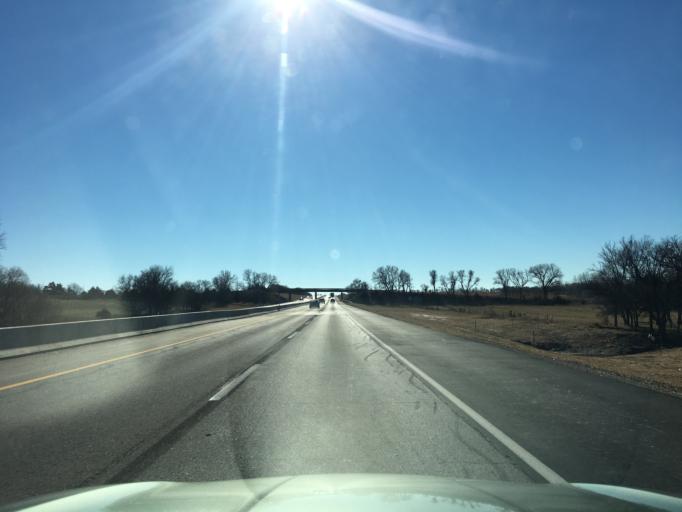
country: US
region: Kansas
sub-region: Sumner County
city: Wellington
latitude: 37.0895
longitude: -97.3387
